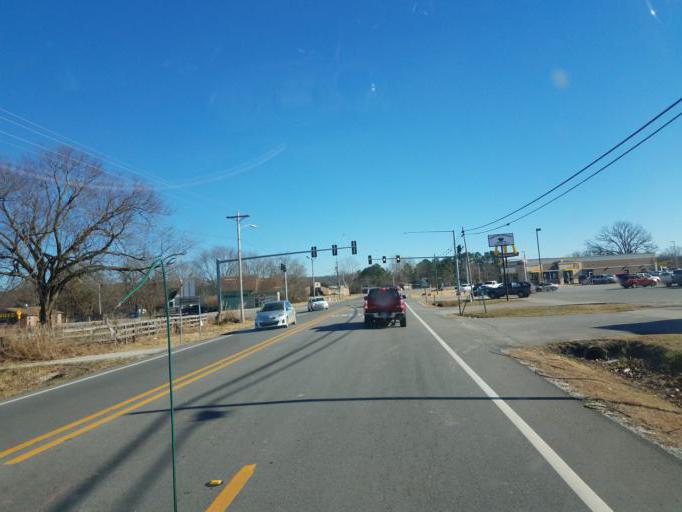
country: US
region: Arkansas
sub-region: Washington County
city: Elkins
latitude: 36.0286
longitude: -94.0236
